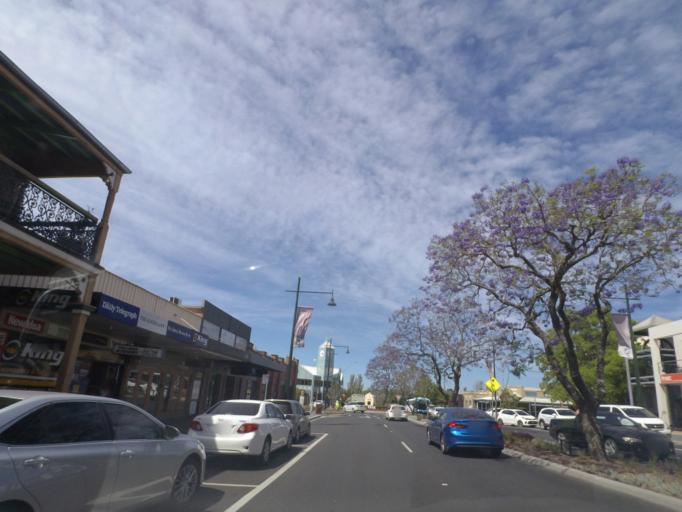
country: AU
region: New South Wales
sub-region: Camden
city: Elderslie
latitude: -34.0540
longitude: 150.6972
